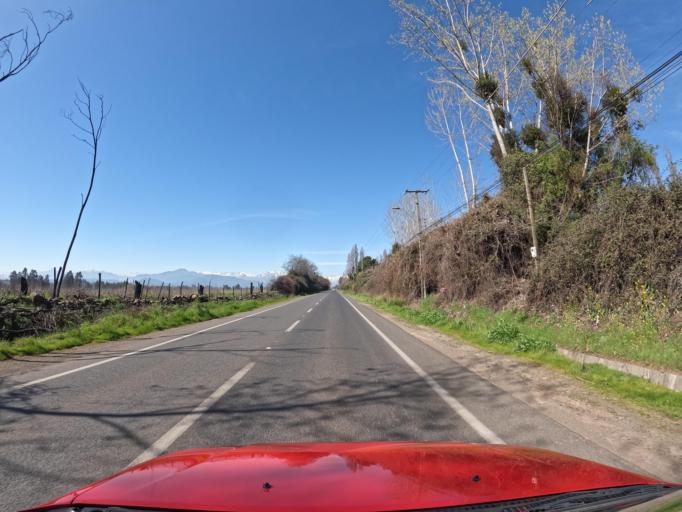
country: CL
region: Maule
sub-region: Provincia de Curico
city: Teno
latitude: -34.9638
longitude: -71.0654
